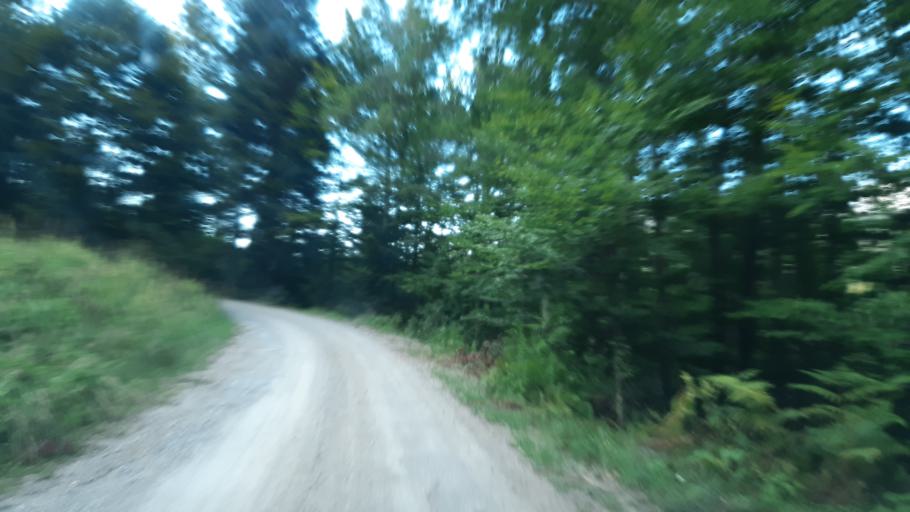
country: SI
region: Dolenjske Toplice
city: Dolenjske Toplice
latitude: 45.6707
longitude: 14.9832
